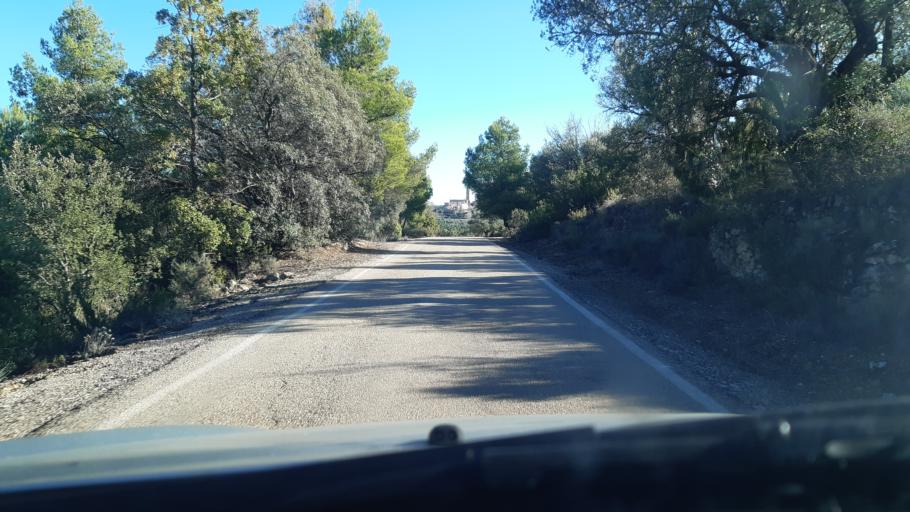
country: ES
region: Aragon
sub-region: Provincia de Teruel
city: Fornoles
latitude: 40.9047
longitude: -0.0111
